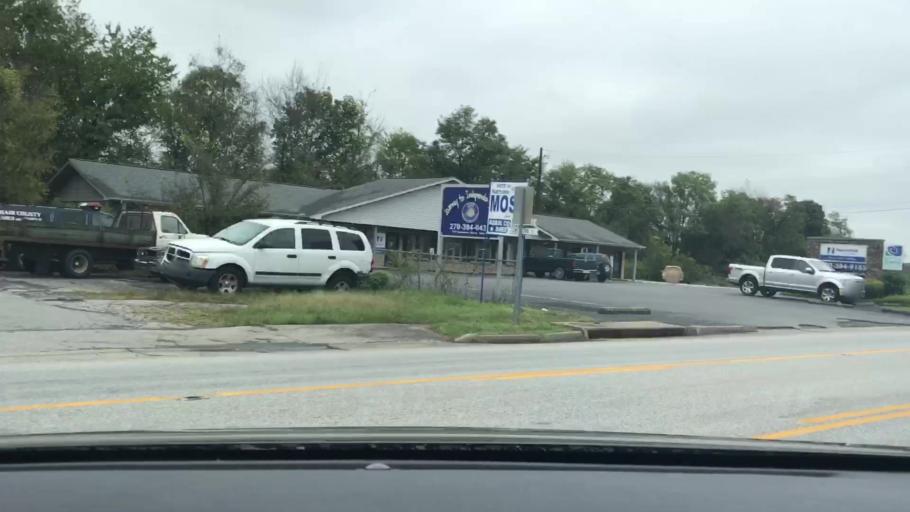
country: US
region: Kentucky
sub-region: Adair County
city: Columbia
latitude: 37.0909
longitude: -85.3045
